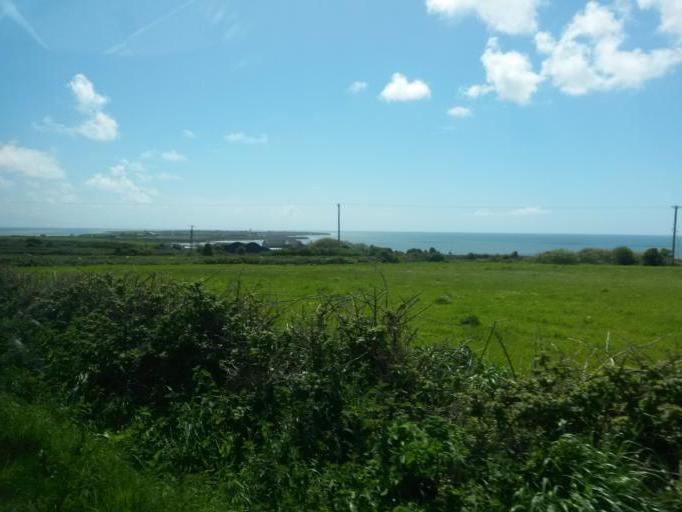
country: IE
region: Munster
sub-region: Waterford
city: Dunmore East
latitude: 52.1685
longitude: -6.8953
